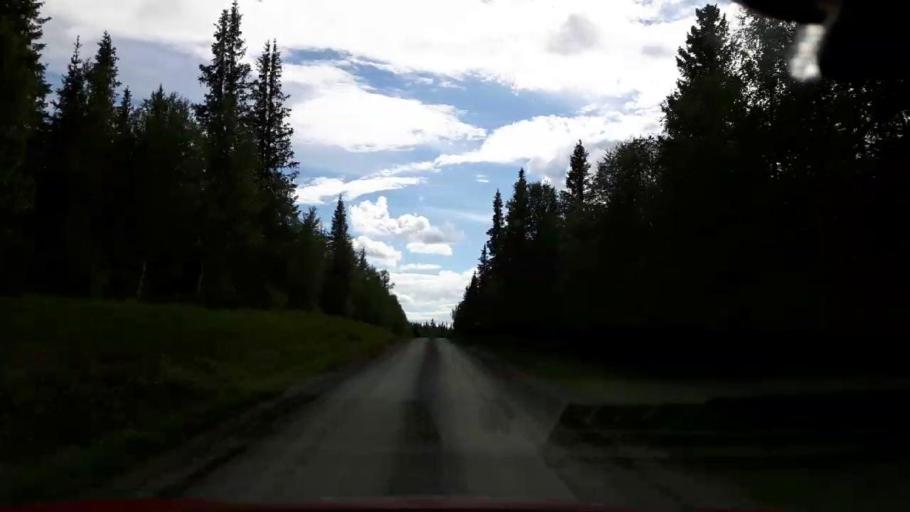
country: SE
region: Jaemtland
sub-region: Krokoms Kommun
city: Valla
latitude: 63.8637
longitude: 14.1113
